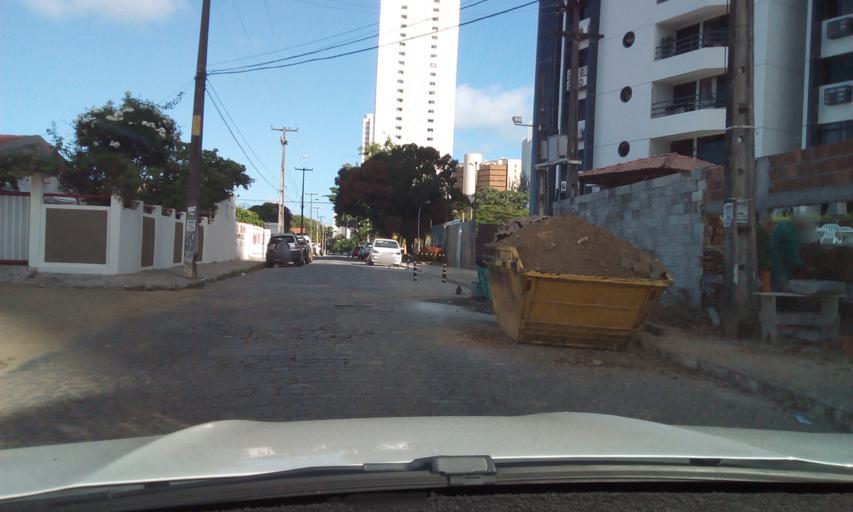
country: BR
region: Paraiba
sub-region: Joao Pessoa
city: Joao Pessoa
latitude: -7.1138
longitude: -34.8394
